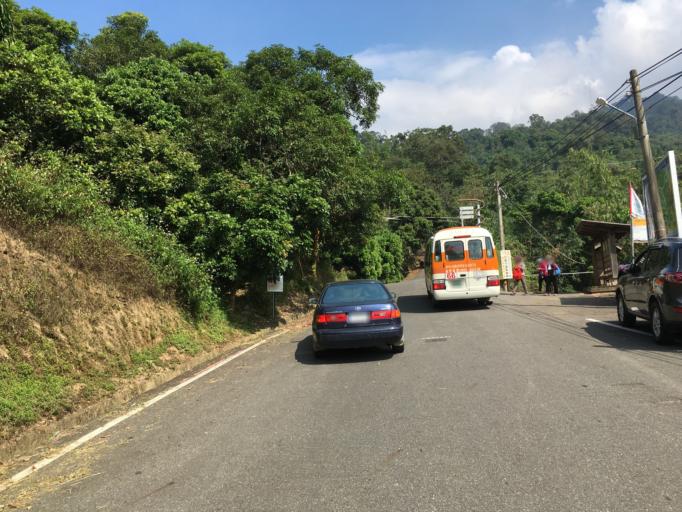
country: TW
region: Taiwan
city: Fengyuan
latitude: 24.1797
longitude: 120.7848
